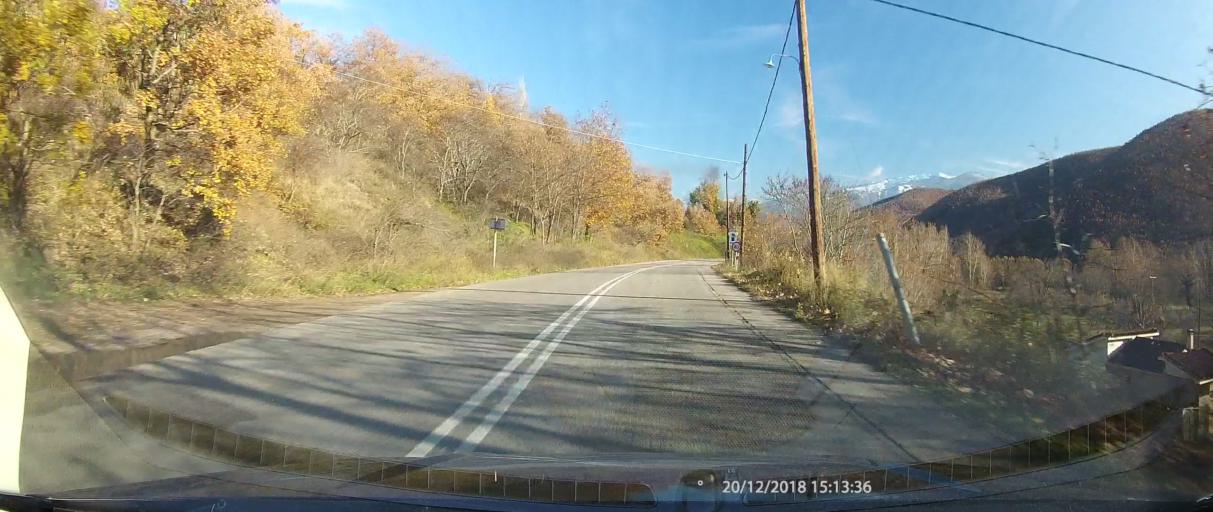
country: GR
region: Central Greece
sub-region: Nomos Fthiotidos
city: Makrakomi
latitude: 38.9325
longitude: 21.9697
